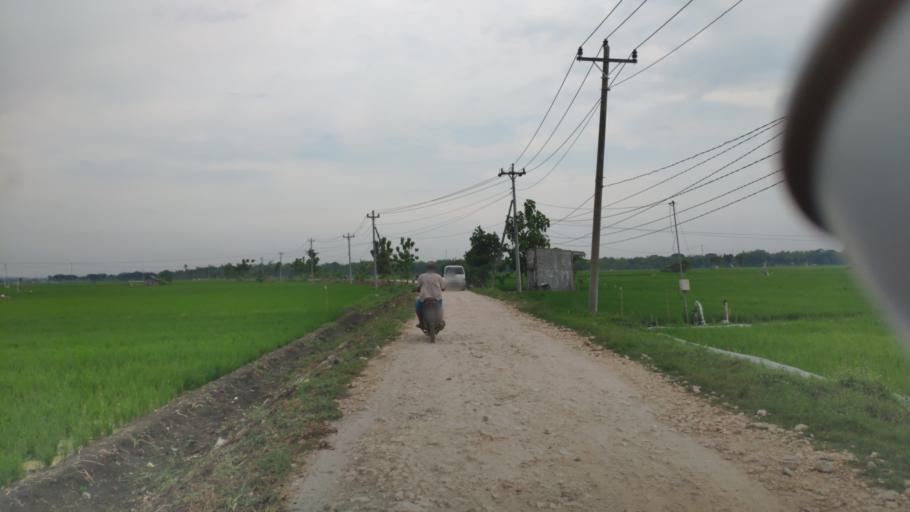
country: ID
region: Central Java
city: Gondel
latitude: -7.2157
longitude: 111.4960
